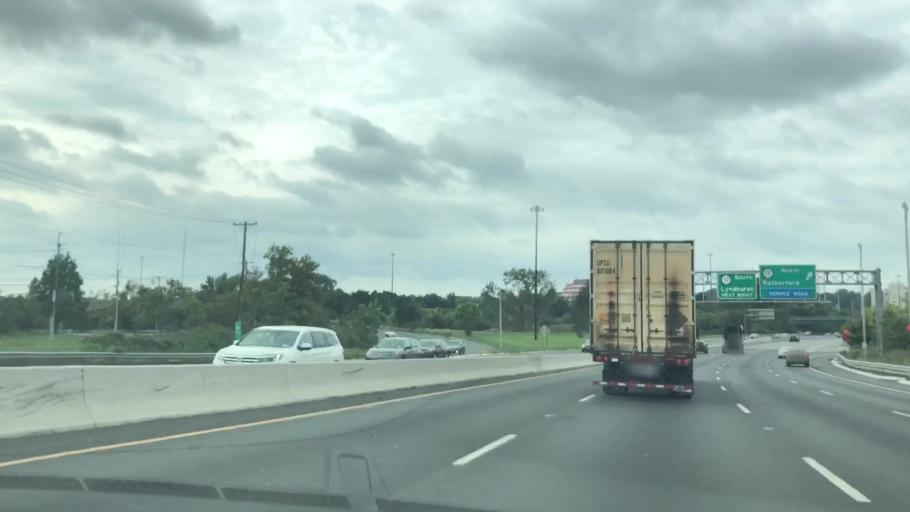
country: US
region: New Jersey
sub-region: Bergen County
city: Rutherford
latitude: 40.8105
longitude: -74.0966
